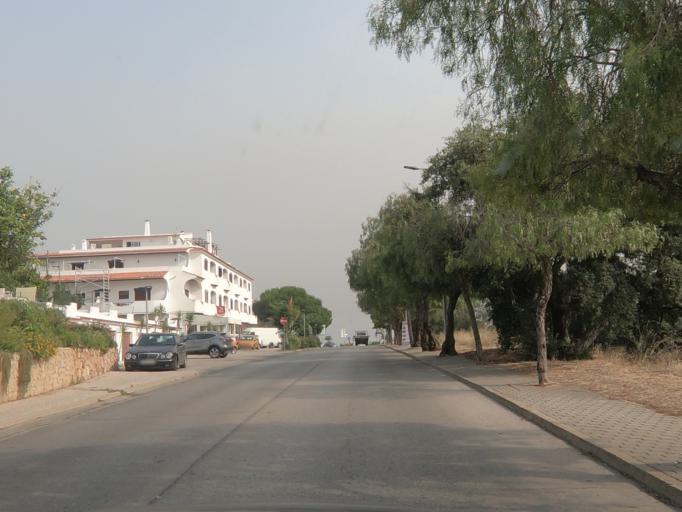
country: PT
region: Faro
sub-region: Silves
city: Armacao de Pera
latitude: 37.1233
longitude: -8.4010
